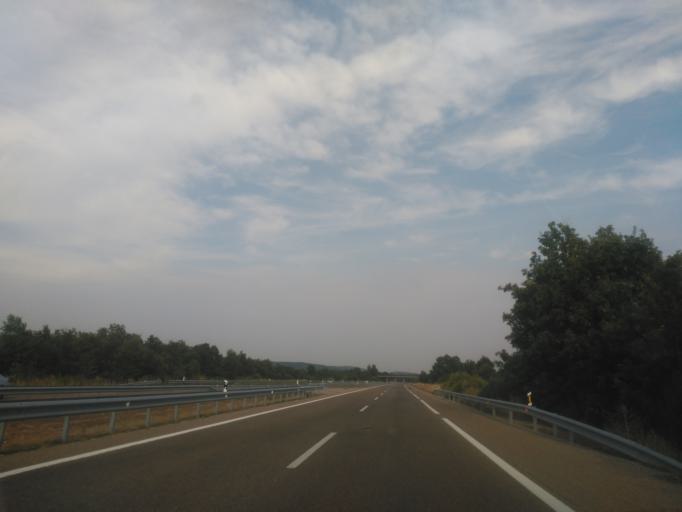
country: ES
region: Castille and Leon
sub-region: Provincia de Zamora
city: Asturianos
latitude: 42.0389
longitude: -6.4532
